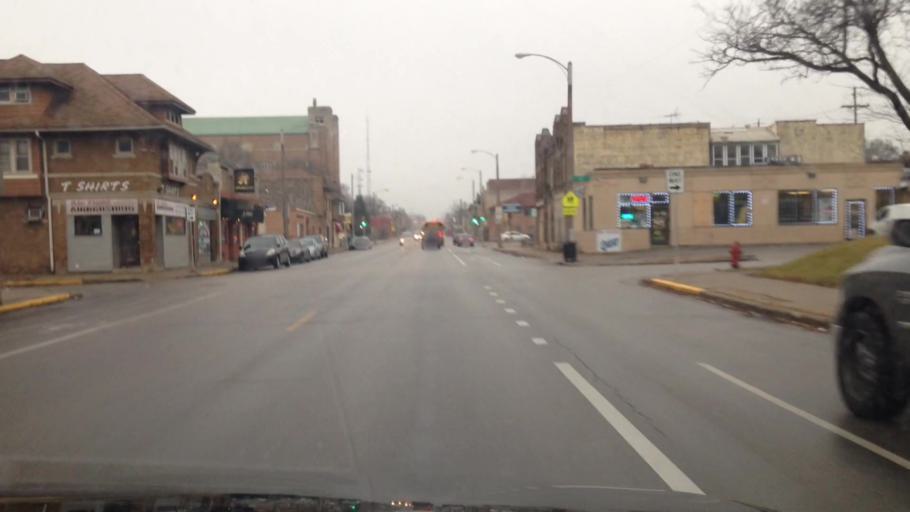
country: US
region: Wisconsin
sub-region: Milwaukee County
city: Wauwatosa
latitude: 43.0680
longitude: -87.9758
